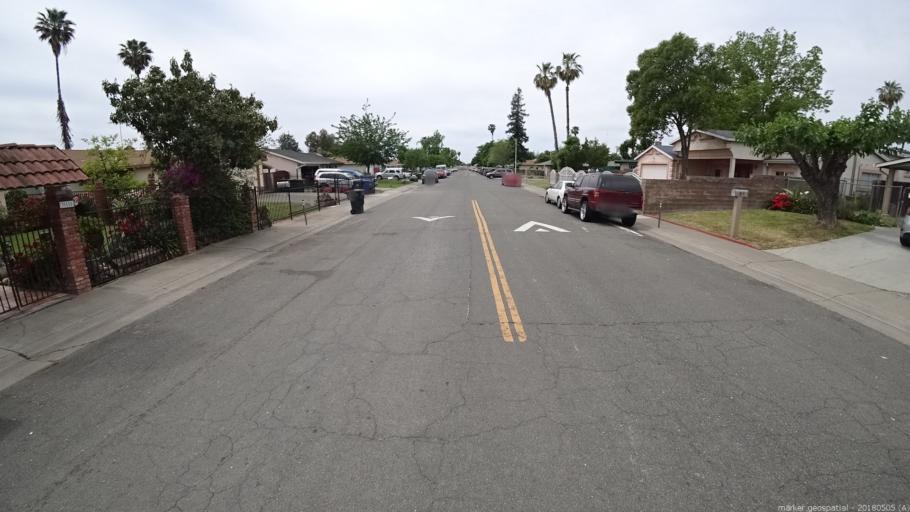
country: US
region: California
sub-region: Sacramento County
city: Rio Linda
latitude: 38.6425
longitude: -121.4612
